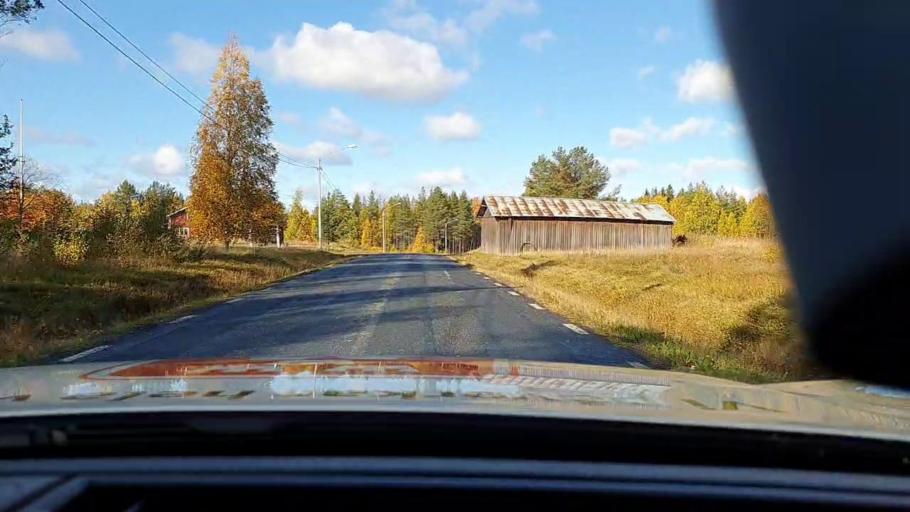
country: SE
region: Vaesterbotten
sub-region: Skelleftea Kommun
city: Langsele
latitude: 65.0118
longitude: 20.0825
